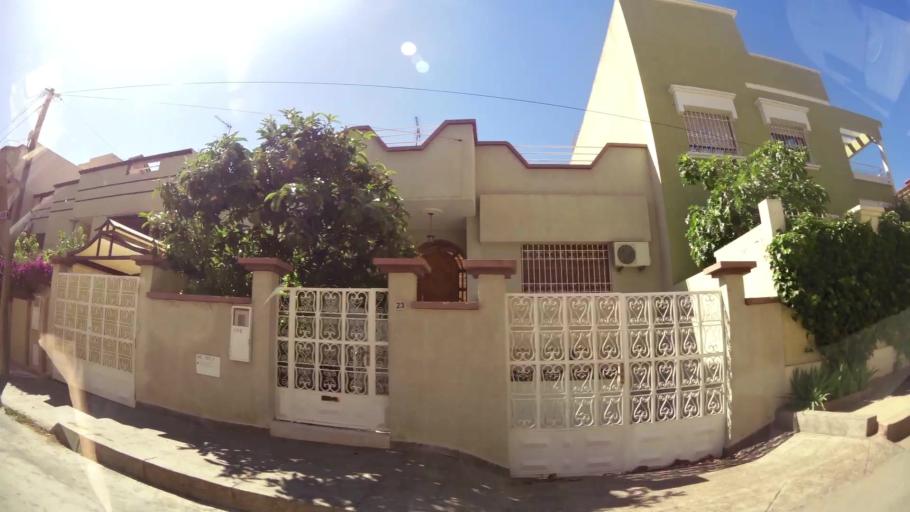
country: MA
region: Oriental
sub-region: Oujda-Angad
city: Oujda
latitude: 34.6581
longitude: -1.8874
